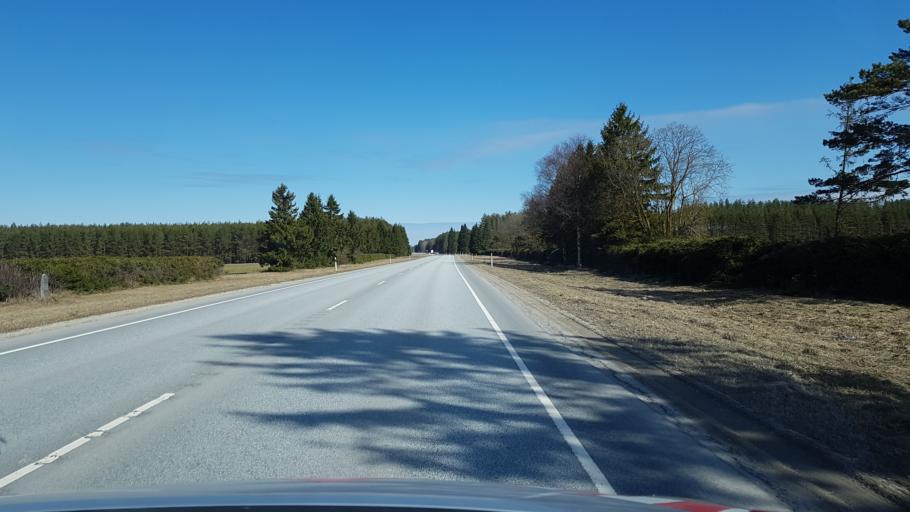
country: EE
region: Laeaene-Virumaa
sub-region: Viru-Nigula vald
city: Kunda
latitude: 59.3911
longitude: 26.6193
